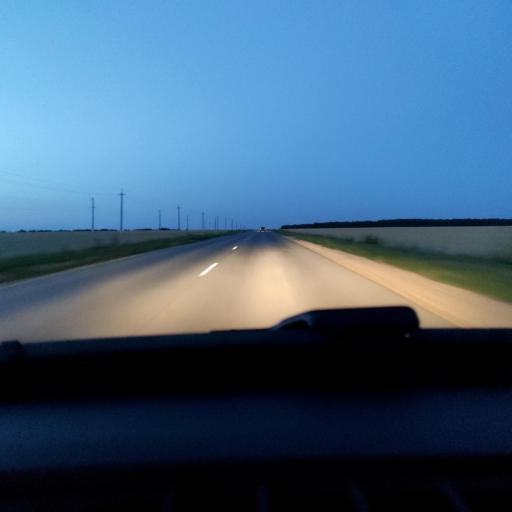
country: RU
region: Lipetsk
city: Zadonsk
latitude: 52.3022
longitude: 38.8628
